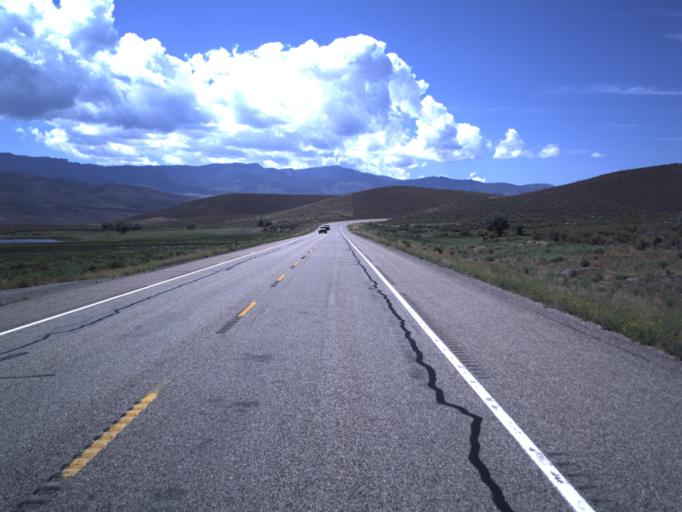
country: US
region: Utah
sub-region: Piute County
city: Junction
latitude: 38.2223
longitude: -112.2198
